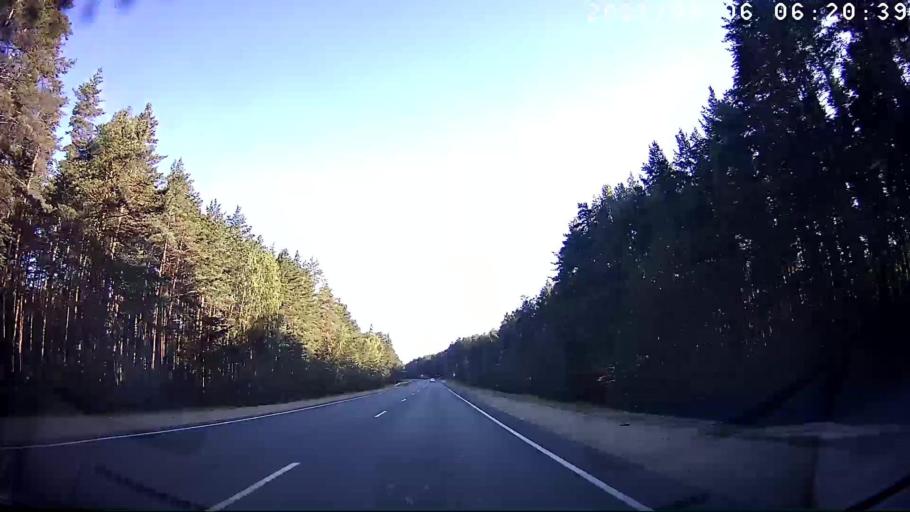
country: RU
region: Mariy-El
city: Pomary
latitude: 56.0575
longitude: 48.3720
